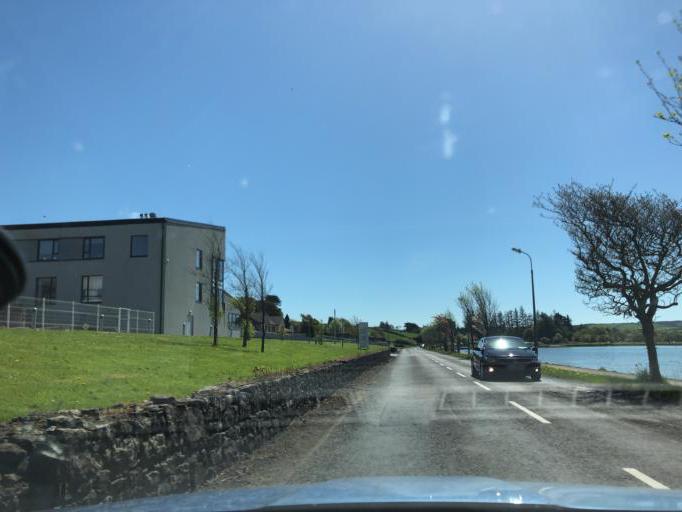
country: IE
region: Connaught
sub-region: County Galway
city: Loughrea
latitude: 53.1894
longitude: -8.5650
